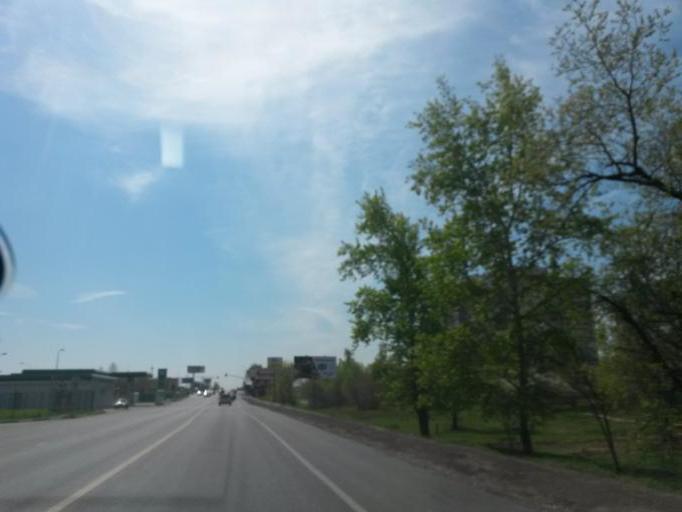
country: RU
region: Moskovskaya
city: Shcherbinka
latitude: 55.5019
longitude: 37.5718
